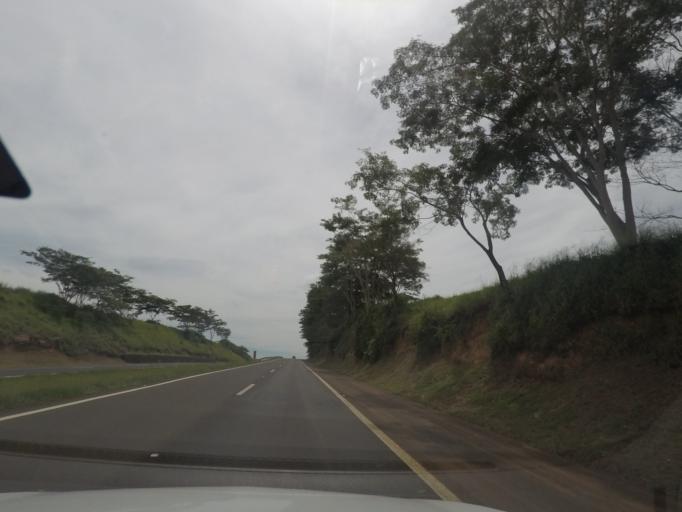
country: BR
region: Sao Paulo
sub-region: Bebedouro
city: Bebedouro
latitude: -21.0246
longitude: -48.4226
